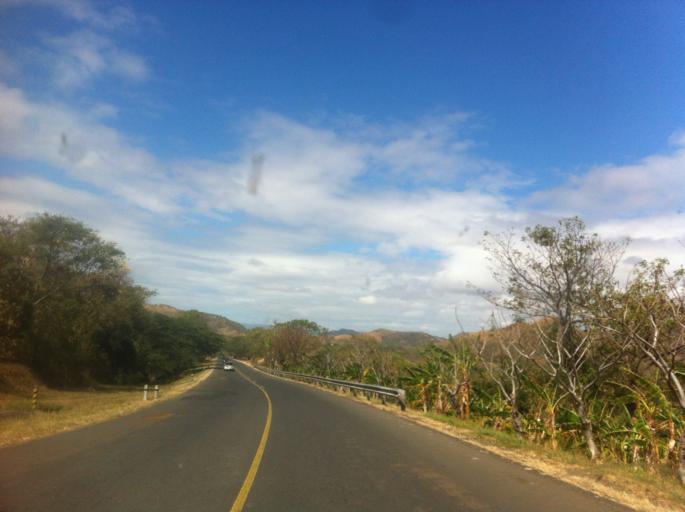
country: NI
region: Chontales
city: Acoyapa
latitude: 12.0087
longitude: -85.2293
